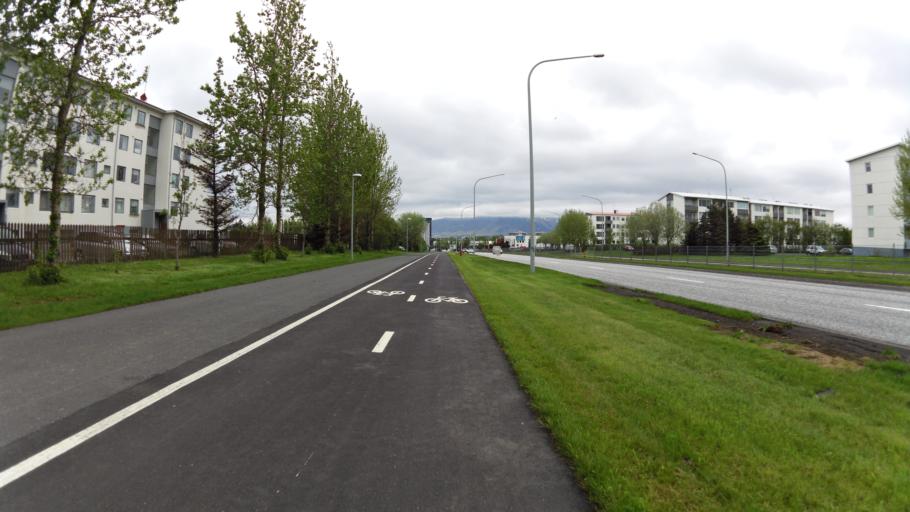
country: IS
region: Capital Region
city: Reykjavik
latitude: 64.1365
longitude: -21.8957
